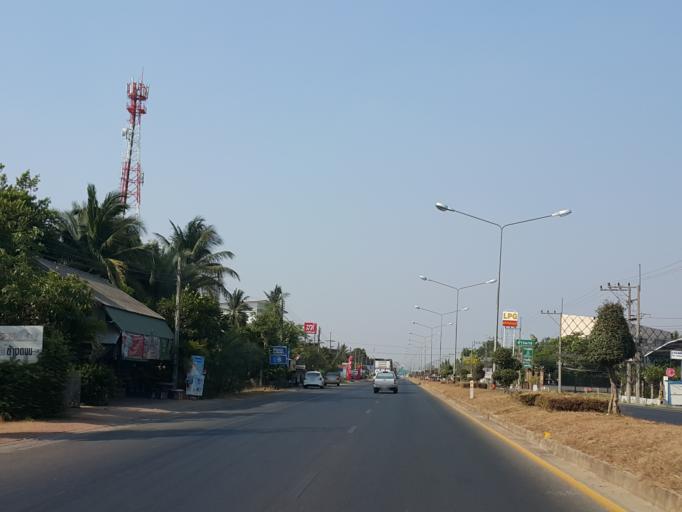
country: TH
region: Phitsanulok
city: Phitsanulok
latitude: 16.8367
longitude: 100.3384
